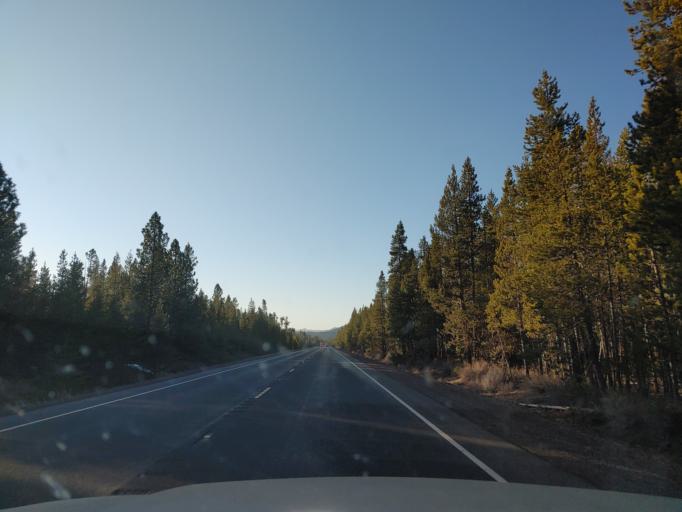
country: US
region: Oregon
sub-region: Deschutes County
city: La Pine
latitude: 43.3981
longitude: -121.8187
